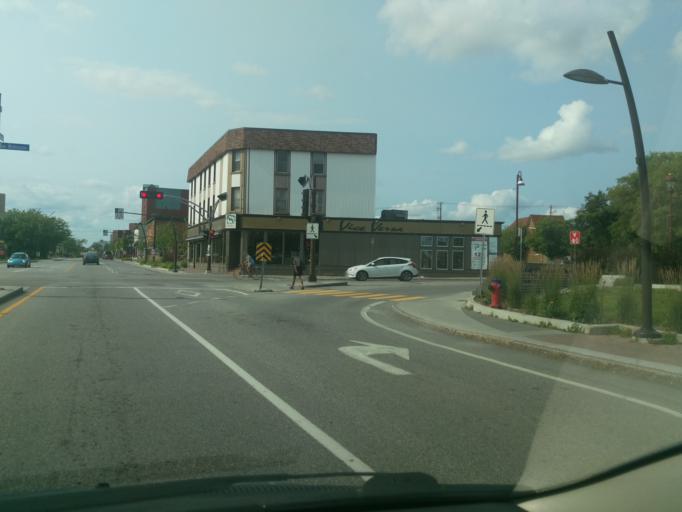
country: CA
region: Ontario
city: Ottawa
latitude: 45.4256
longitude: -75.7235
